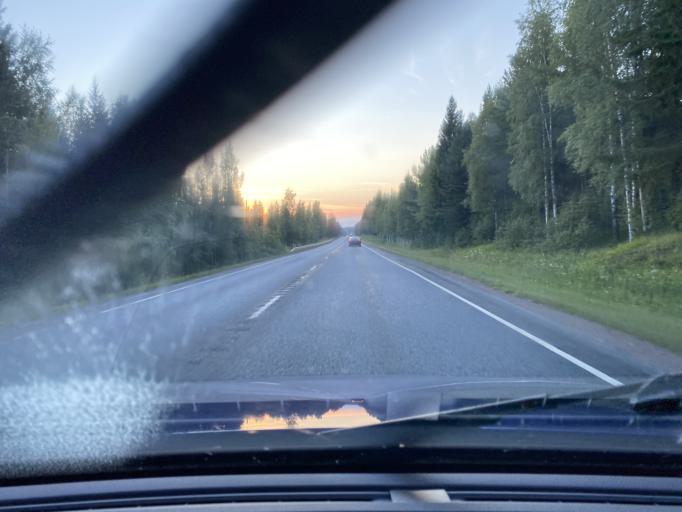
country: FI
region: Pirkanmaa
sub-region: Luoteis-Pirkanmaa
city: Ikaalinen
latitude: 61.7982
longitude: 22.9769
